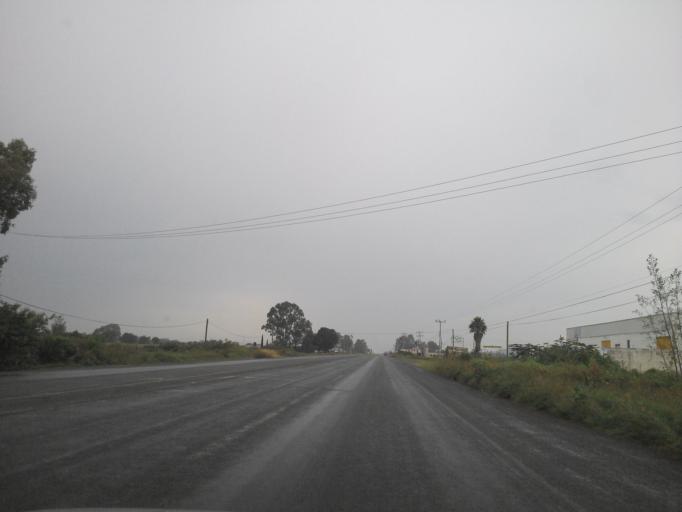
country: MX
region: Jalisco
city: Capilla de Guadalupe
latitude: 20.8370
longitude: -102.6057
